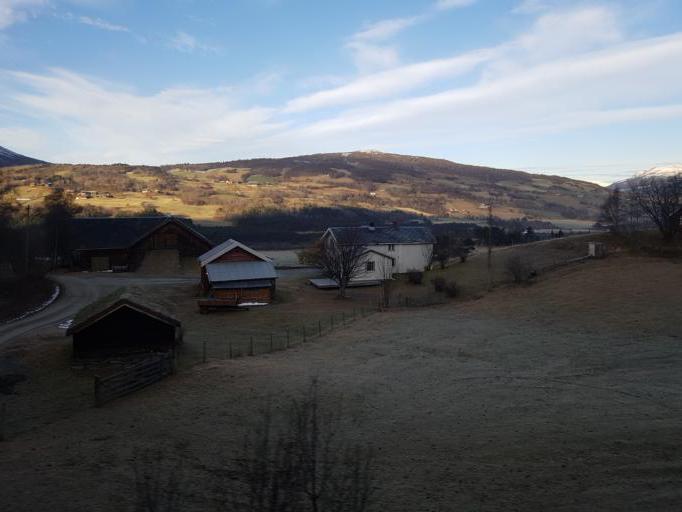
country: NO
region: Sor-Trondelag
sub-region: Oppdal
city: Oppdal
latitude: 62.5304
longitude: 9.6139
